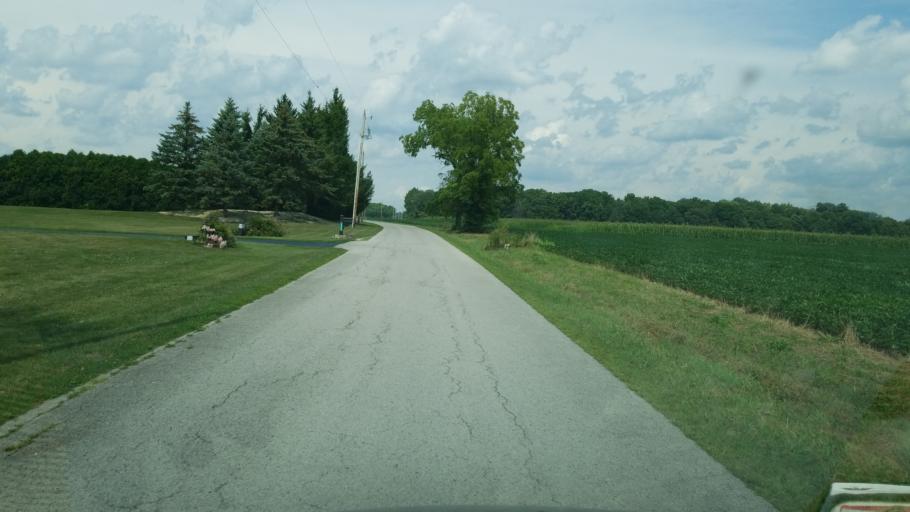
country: US
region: Ohio
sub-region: Hancock County
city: Arlington
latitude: 40.9475
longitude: -83.5418
